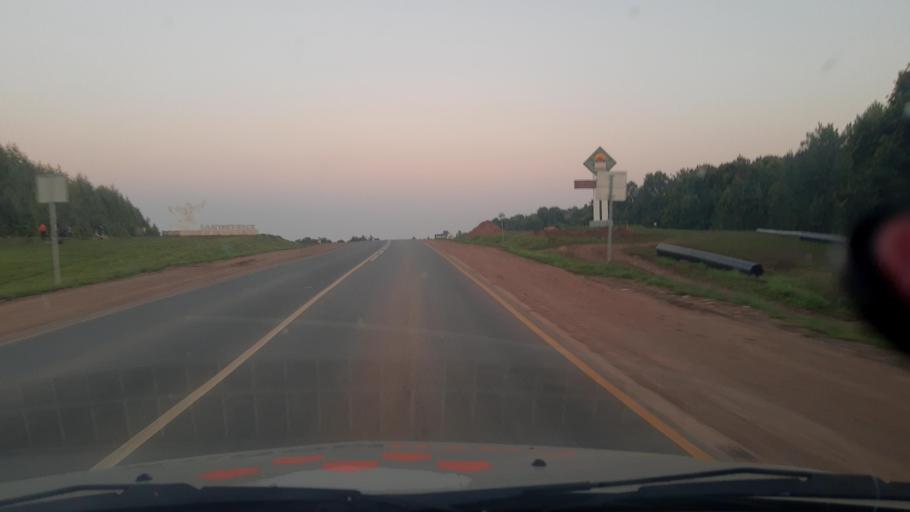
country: RU
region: Bashkortostan
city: Blagoveshchensk
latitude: 55.0620
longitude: 55.9339
